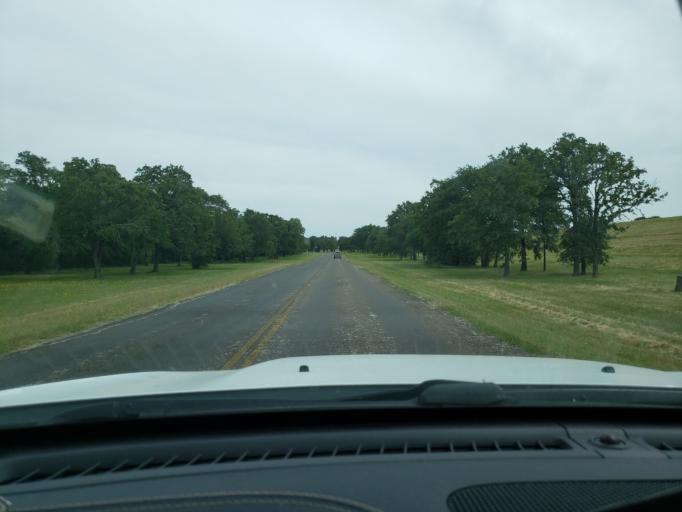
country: US
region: Texas
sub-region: Burleson County
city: Somerville
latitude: 30.3420
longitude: -96.5442
